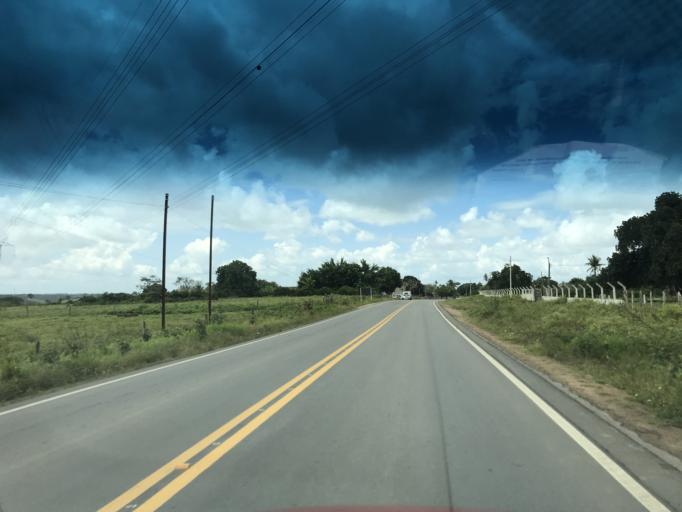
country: BR
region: Bahia
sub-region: Conceicao Do Almeida
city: Conceicao do Almeida
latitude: -12.7252
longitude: -39.2050
